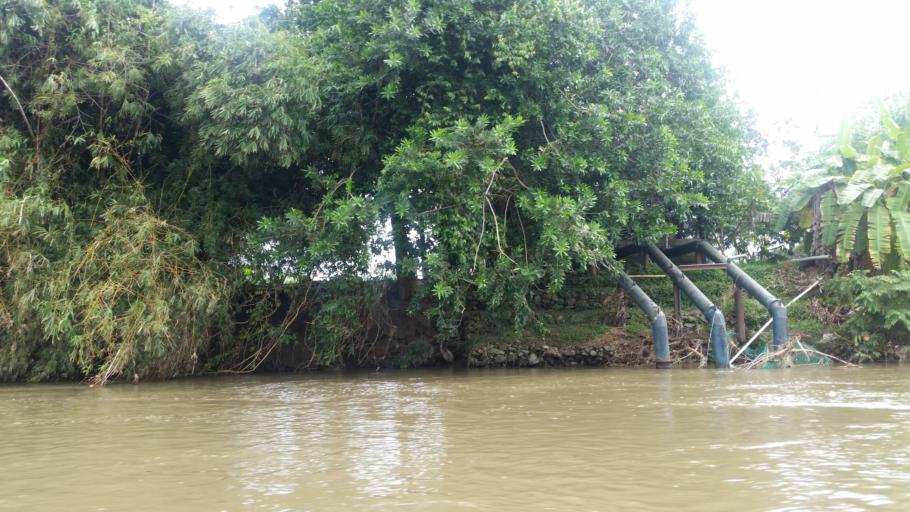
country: CO
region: Magdalena
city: Santa Marta
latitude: 11.2554
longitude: -73.7636
